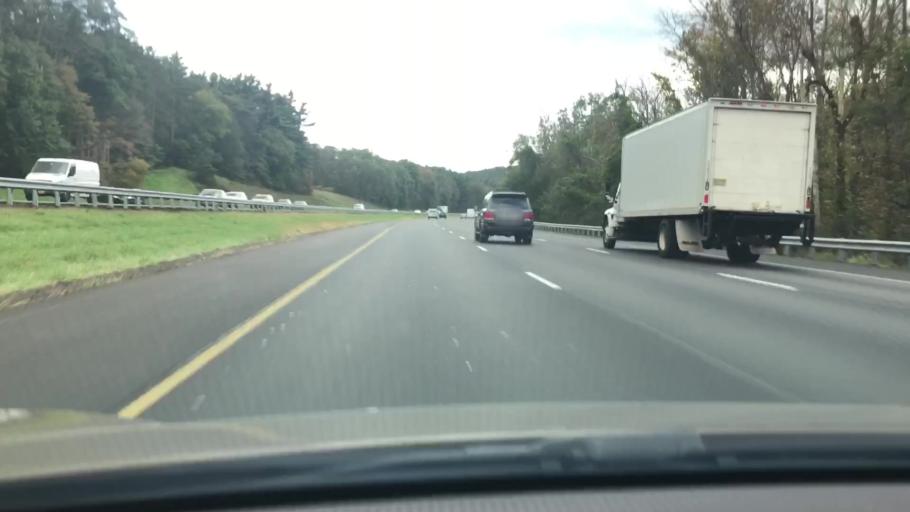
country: US
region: New York
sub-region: Orange County
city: Harriman
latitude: 41.2380
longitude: -74.1729
